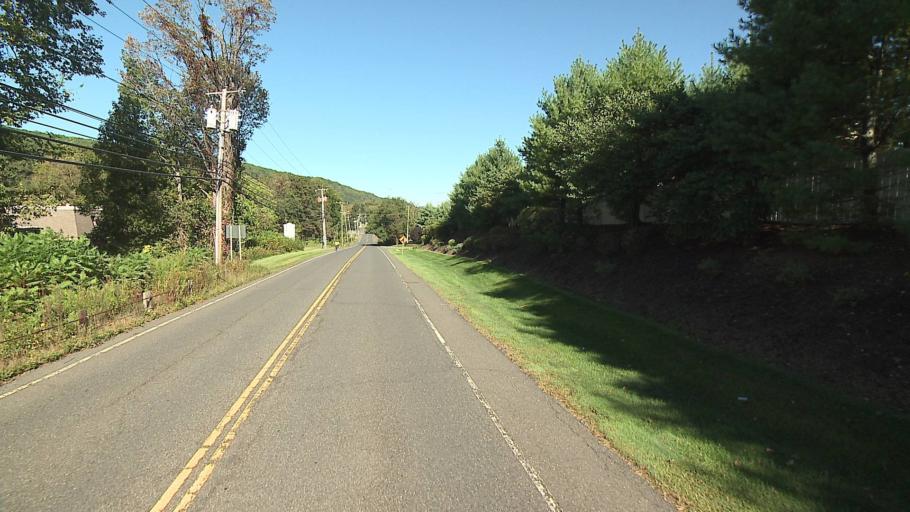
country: US
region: Connecticut
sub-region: Litchfield County
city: New Milford
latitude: 41.4903
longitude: -73.4144
